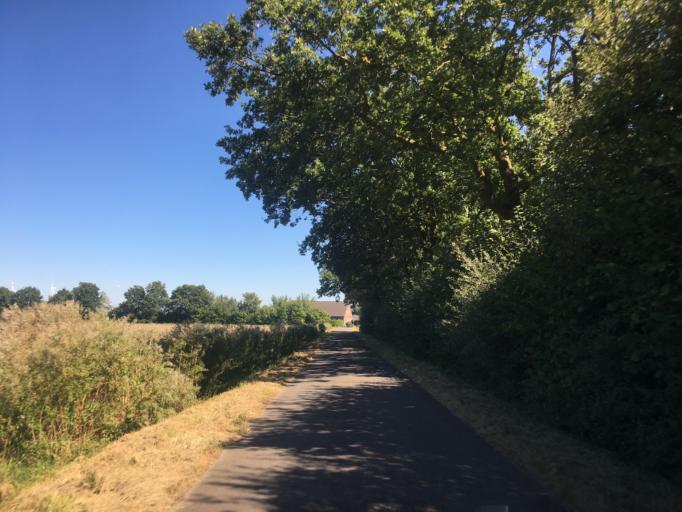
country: DE
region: North Rhine-Westphalia
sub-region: Regierungsbezirk Munster
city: Greven
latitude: 52.0277
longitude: 7.5578
